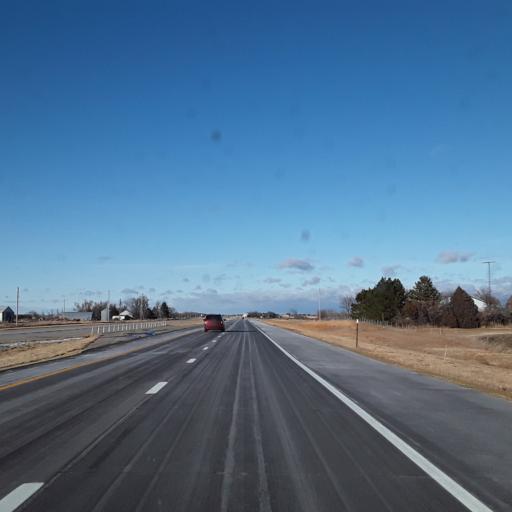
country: US
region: Kansas
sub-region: Republic County
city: Belleville
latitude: 39.7711
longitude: -97.6515
